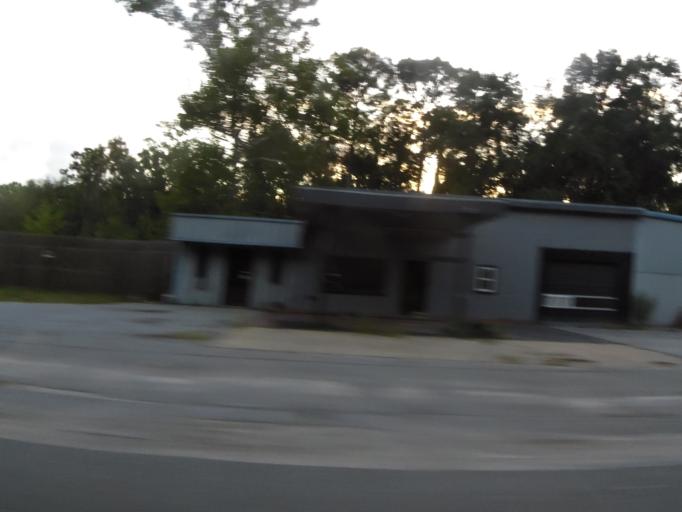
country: US
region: Georgia
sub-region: Camden County
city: Kingsland
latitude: 30.7906
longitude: -81.6884
